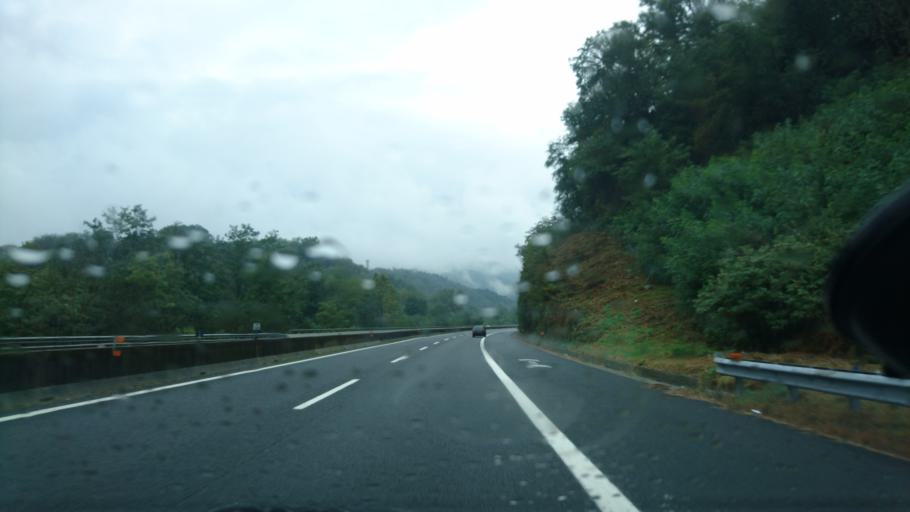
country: IT
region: Piedmont
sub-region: Provincia di Novara
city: Invorio
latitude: 45.7643
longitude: 8.4961
